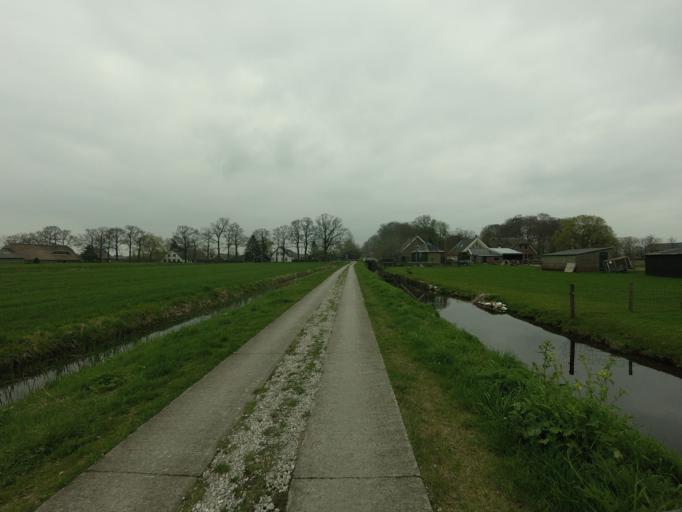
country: NL
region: Utrecht
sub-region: Gemeente De Bilt
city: De Bilt
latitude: 52.1483
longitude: 5.1559
